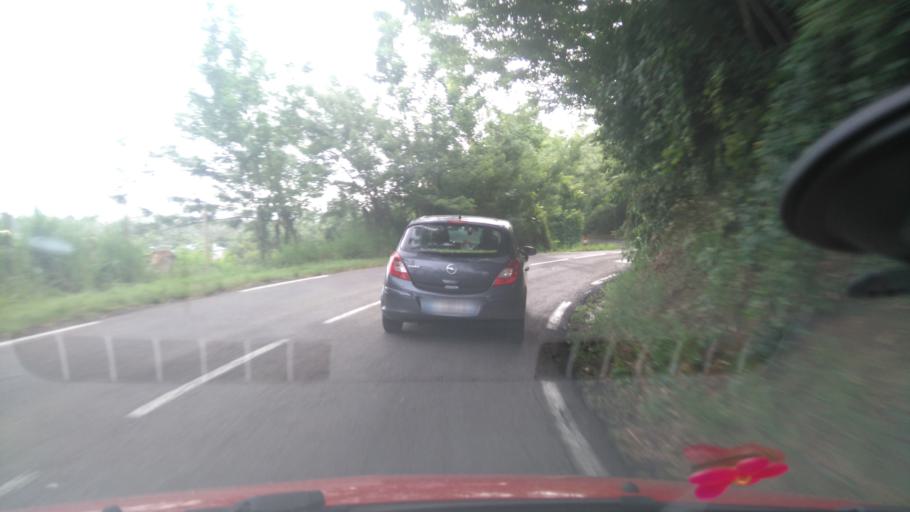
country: MQ
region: Martinique
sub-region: Martinique
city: Saint-Esprit
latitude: 14.5532
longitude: -60.9593
